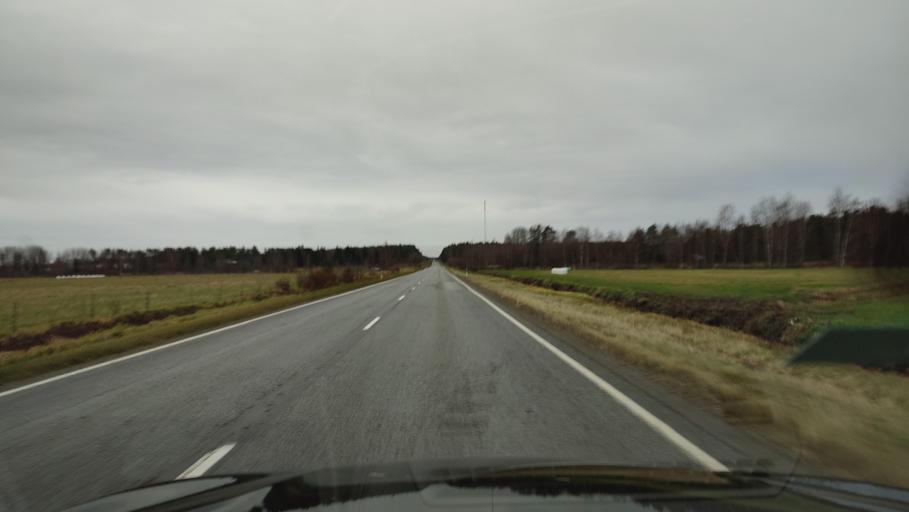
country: FI
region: Ostrobothnia
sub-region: Sydosterbotten
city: Naerpes
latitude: 62.4038
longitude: 21.3853
